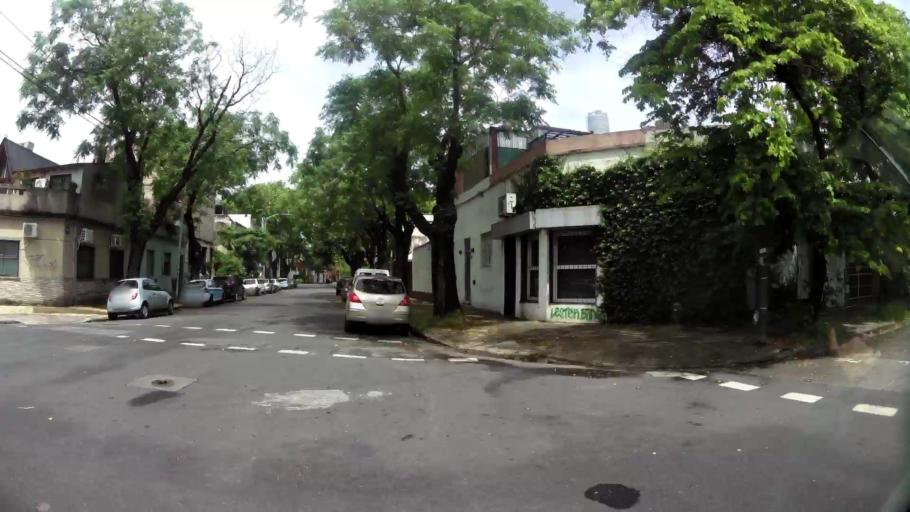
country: AR
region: Buenos Aires F.D.
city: Colegiales
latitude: -34.5883
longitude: -58.4414
